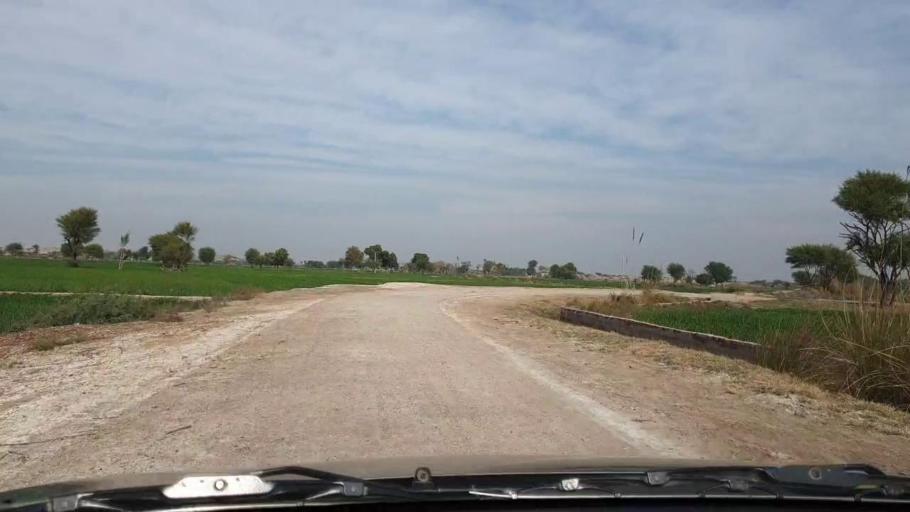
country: PK
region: Sindh
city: Jam Sahib
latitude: 26.2914
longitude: 68.6931
